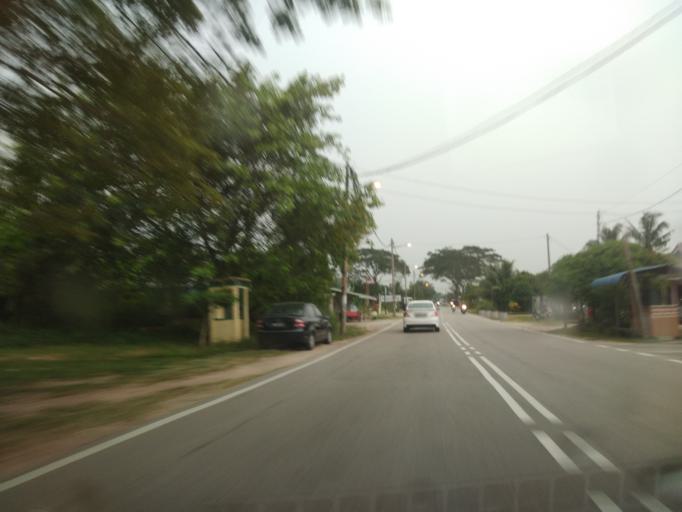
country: MY
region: Penang
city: Permatang Kuching
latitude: 5.4772
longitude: 100.4014
